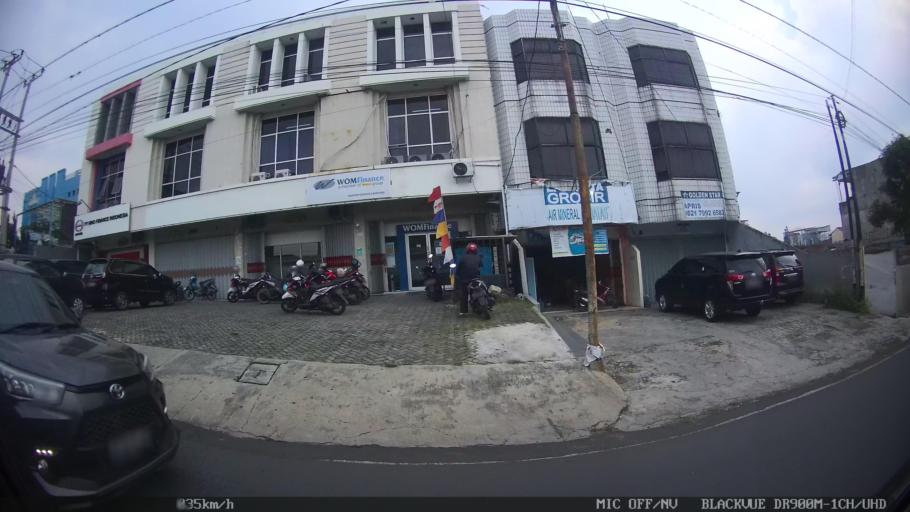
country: ID
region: Lampung
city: Bandarlampung
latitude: -5.4242
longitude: 105.2530
